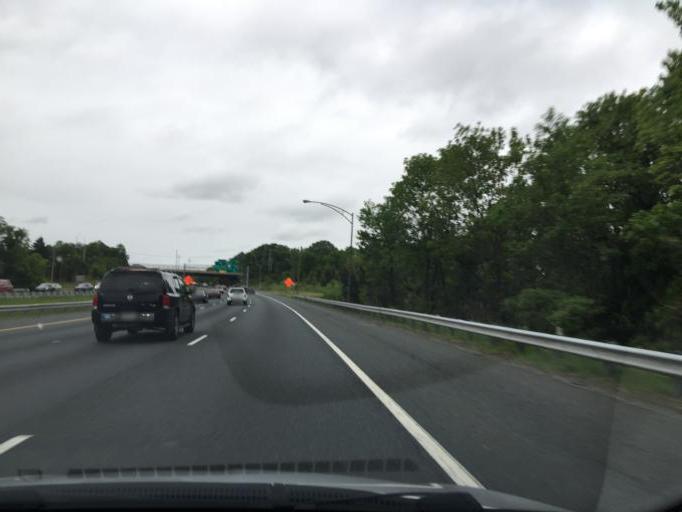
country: US
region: Maryland
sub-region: Baltimore County
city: Overlea
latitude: 39.3717
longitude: -76.5166
